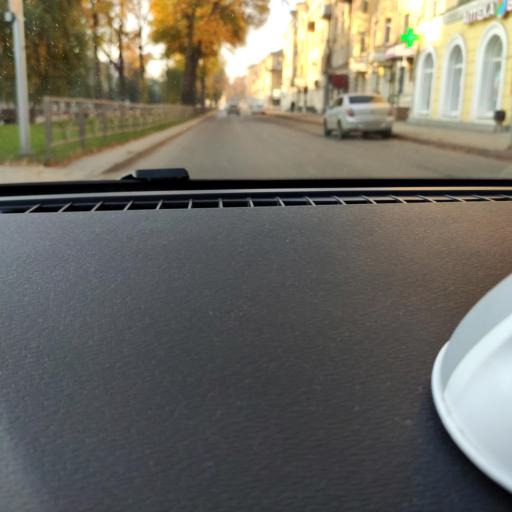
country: RU
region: Samara
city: Petra-Dubrava
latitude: 53.2356
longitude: 50.2770
